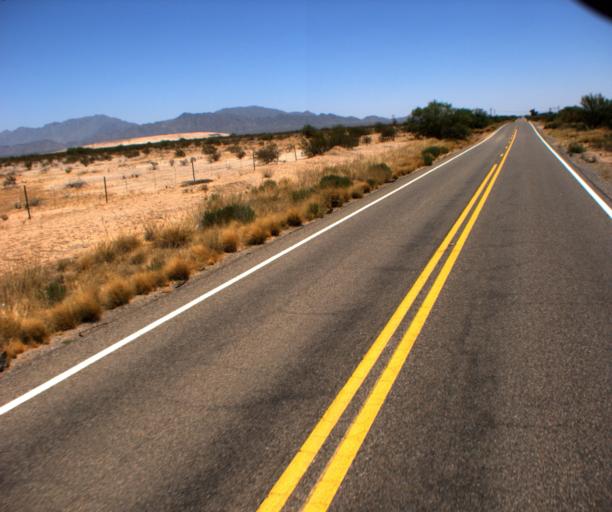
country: US
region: Arizona
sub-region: Pinal County
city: Maricopa
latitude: 33.0448
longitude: -112.3136
